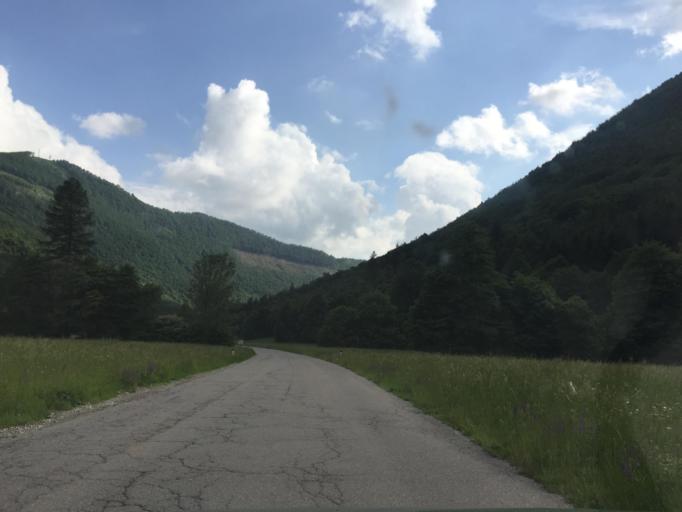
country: SI
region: Nova Gorica
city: Sempas
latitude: 46.0339
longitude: 13.7821
